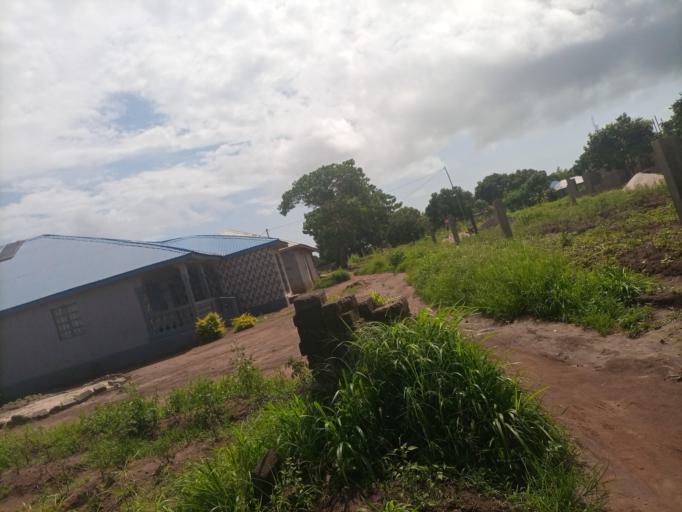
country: SL
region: Northern Province
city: Sawkta
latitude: 8.6370
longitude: -13.2106
